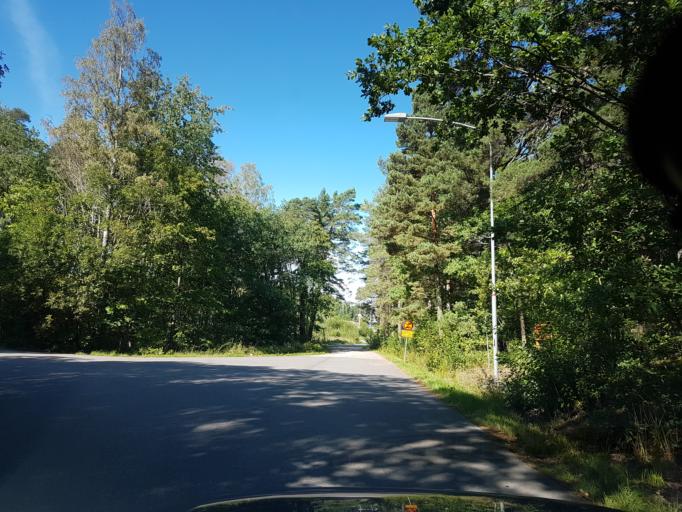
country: SE
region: OEstergoetland
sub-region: Norrkopings Kommun
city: Norrkoping
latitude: 58.5713
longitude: 16.1864
